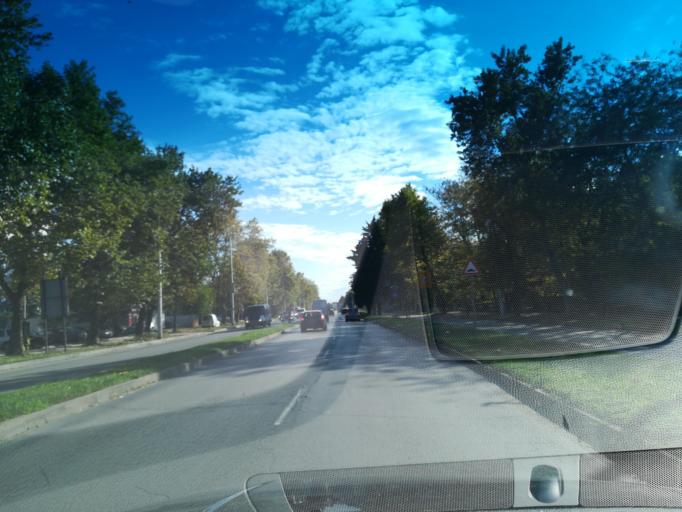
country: BG
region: Stara Zagora
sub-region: Obshtina Stara Zagora
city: Stara Zagora
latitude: 42.4076
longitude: 25.6404
